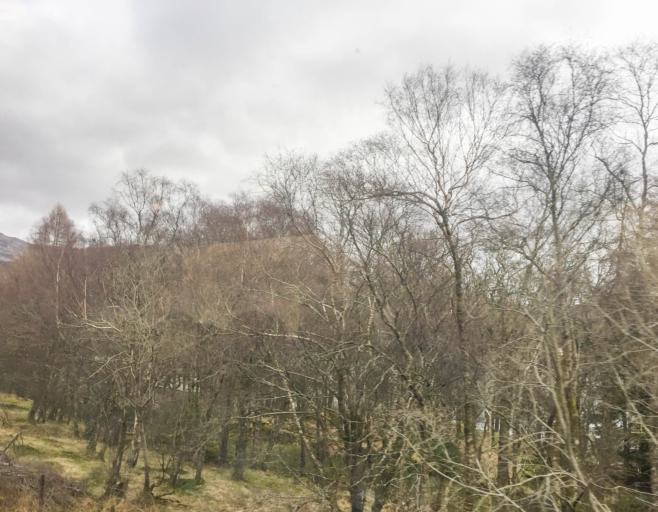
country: GB
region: Scotland
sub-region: Argyll and Bute
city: Garelochhead
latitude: 56.2505
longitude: -4.7139
